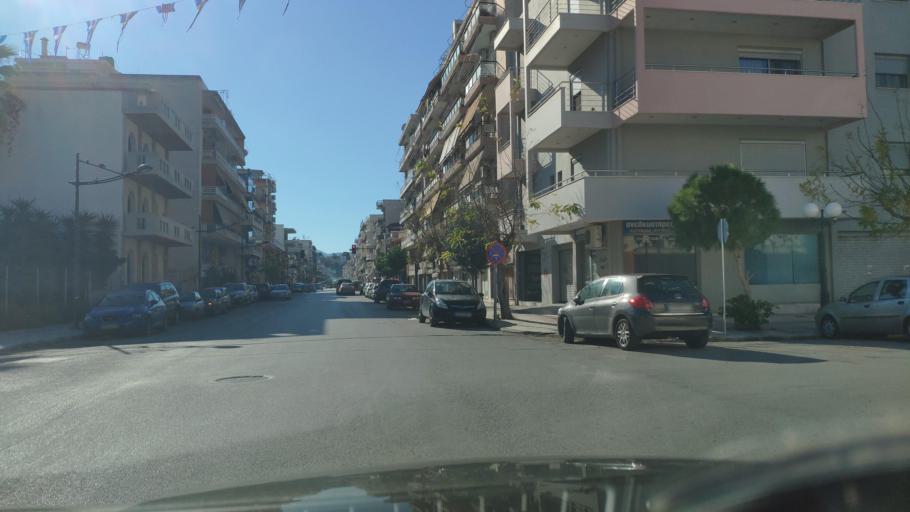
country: GR
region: Peloponnese
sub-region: Nomos Korinthias
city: Korinthos
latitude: 37.9394
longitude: 22.9377
